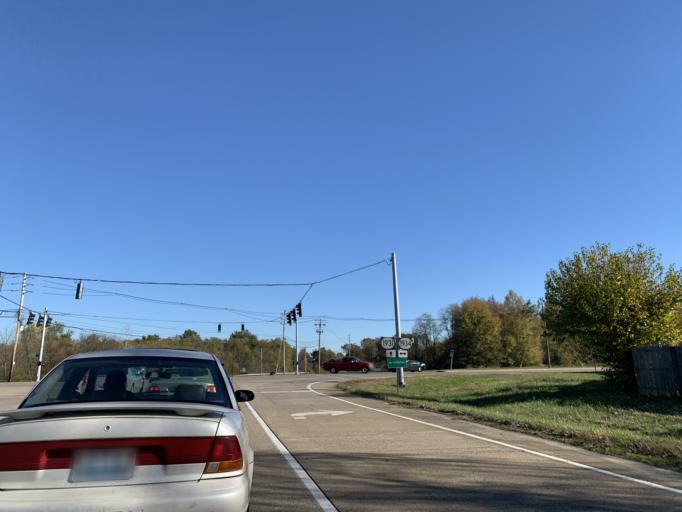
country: US
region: Kentucky
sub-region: Jefferson County
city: Pleasure Ridge Park
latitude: 38.1471
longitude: -85.8871
